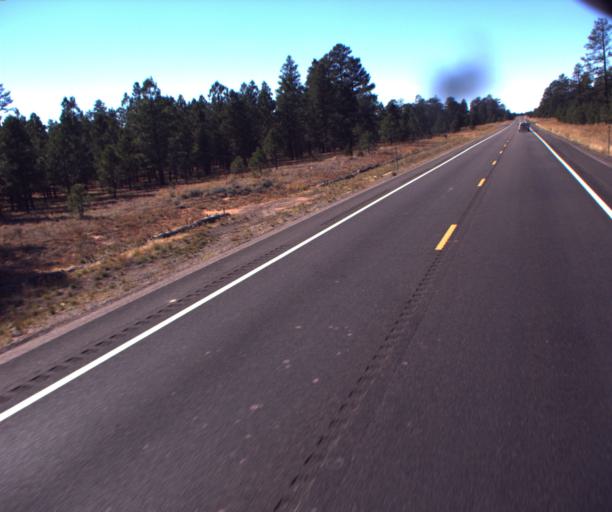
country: US
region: Arizona
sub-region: Apache County
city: Saint Michaels
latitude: 35.6987
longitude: -109.2842
